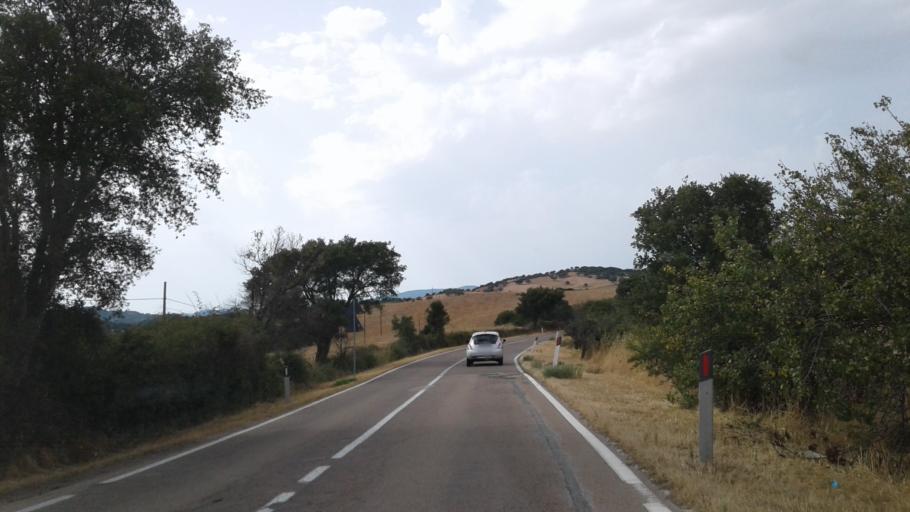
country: IT
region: Sardinia
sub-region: Provincia di Olbia-Tempio
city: Sant'Antonio di Gallura
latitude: 40.9456
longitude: 9.2990
